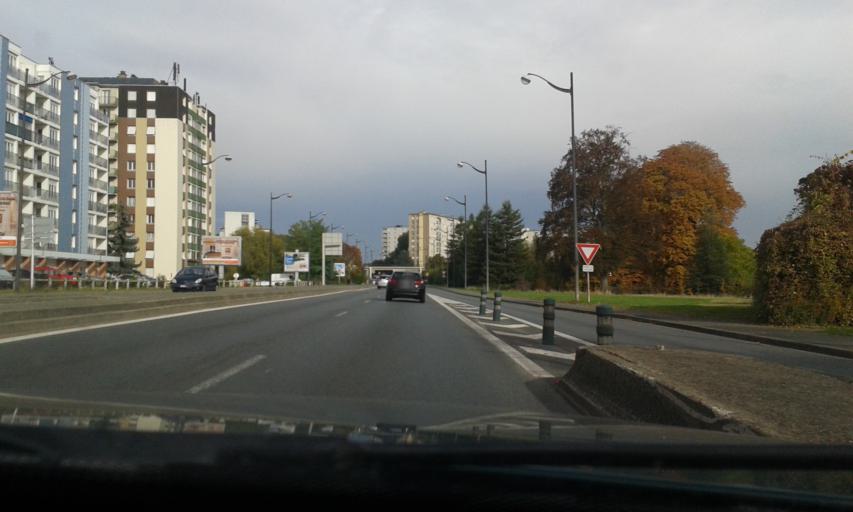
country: FR
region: Centre
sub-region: Departement du Loiret
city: Orleans
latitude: 47.8898
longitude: 1.8953
